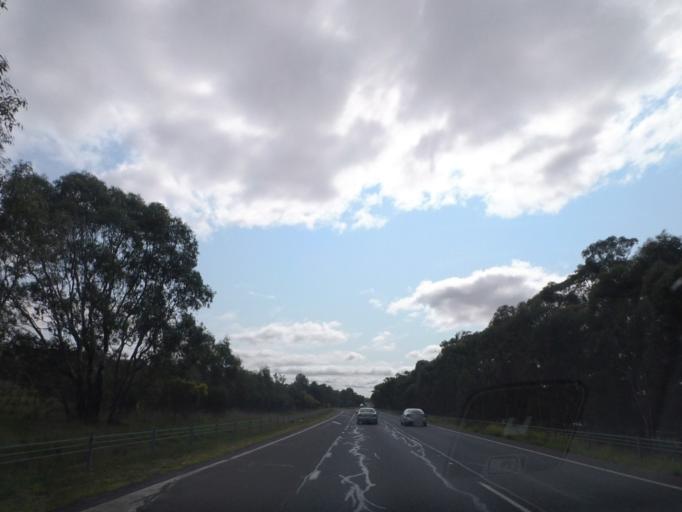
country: AU
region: Victoria
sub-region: Murrindindi
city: Kinglake West
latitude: -37.1135
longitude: 145.0917
